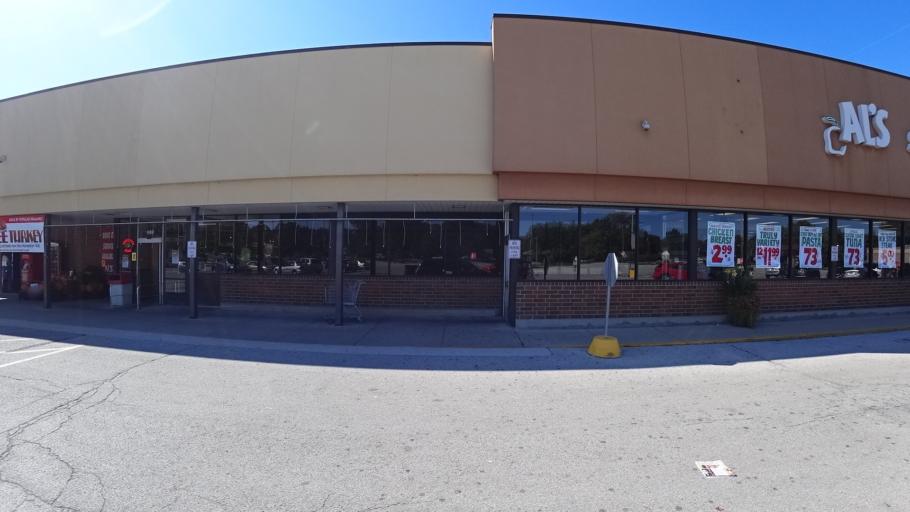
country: US
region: Indiana
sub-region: LaPorte County
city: Michigan City
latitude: 41.6887
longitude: -86.8953
